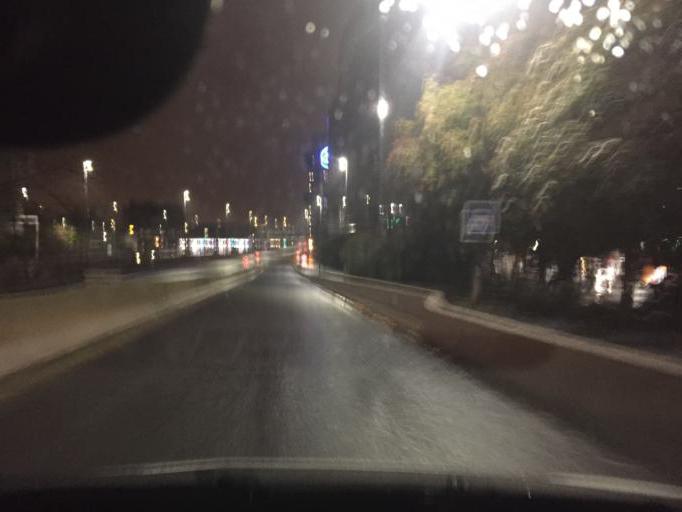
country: FR
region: Ile-de-France
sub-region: Departement du Val-de-Marne
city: Creteil
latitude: 48.7819
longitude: 2.4584
